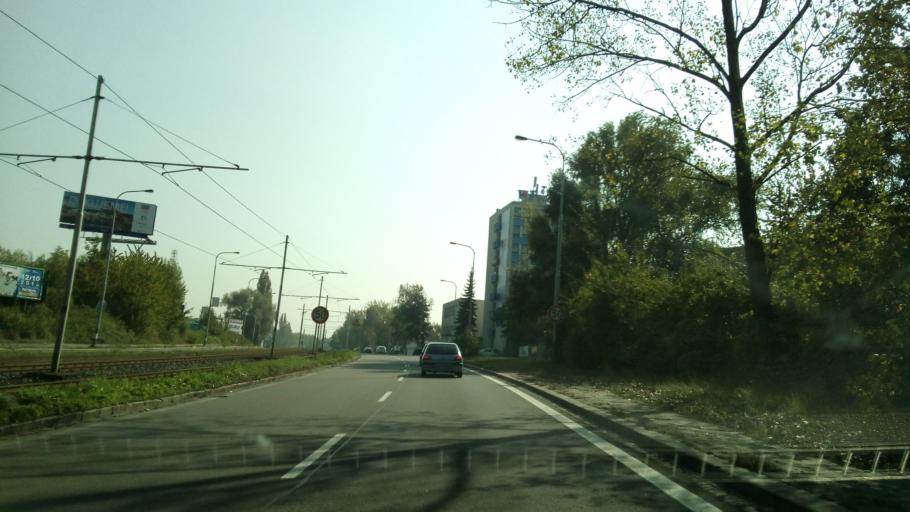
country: CZ
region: Moravskoslezsky
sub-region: Okres Ostrava-Mesto
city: Ostrava
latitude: 49.8159
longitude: 18.2376
